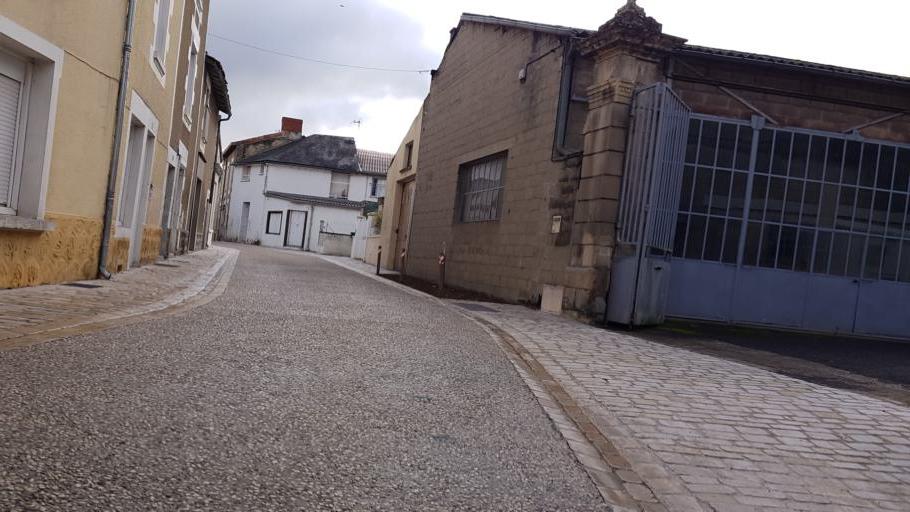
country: FR
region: Poitou-Charentes
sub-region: Departement de la Vienne
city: Chasseneuil-du-Poitou
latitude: 46.6506
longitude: 0.3743
